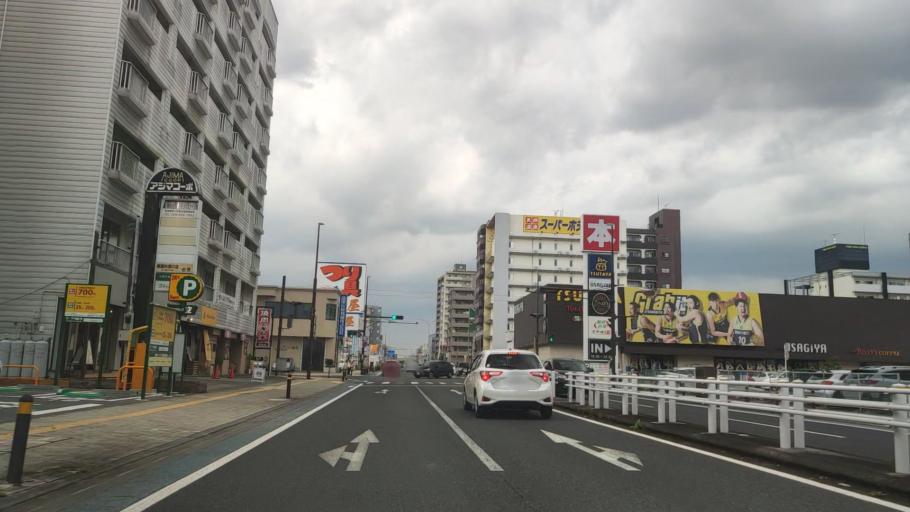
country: JP
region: Tochigi
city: Utsunomiya-shi
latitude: 36.5594
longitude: 139.9037
